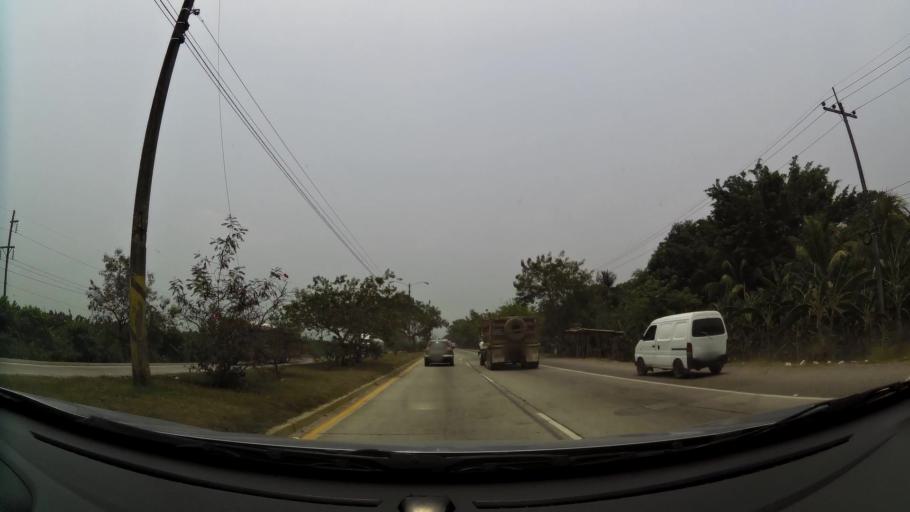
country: HN
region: Yoro
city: El Progreso
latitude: 15.4102
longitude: -87.8404
